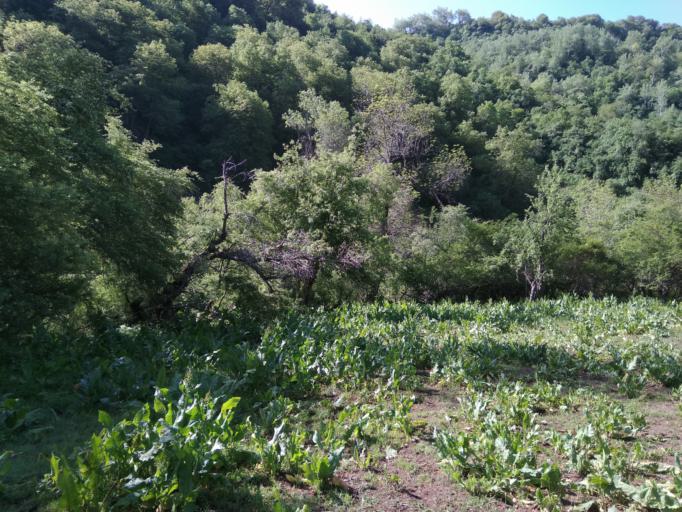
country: KG
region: Jalal-Abad
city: Uch-Terek
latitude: 41.3401
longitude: 73.1458
